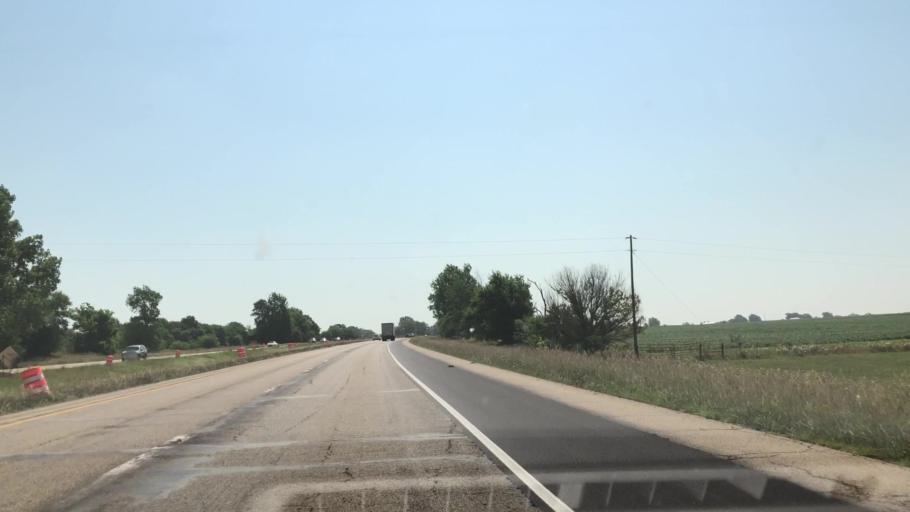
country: US
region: Illinois
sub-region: McLean County
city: Danvers
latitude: 40.6089
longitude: -89.1894
